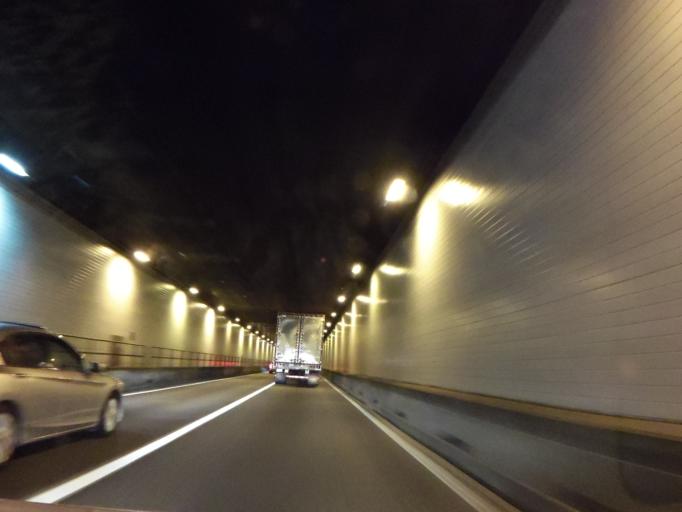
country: US
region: Virginia
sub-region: Bland County
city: Bland
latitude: 37.0383
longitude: -81.1299
